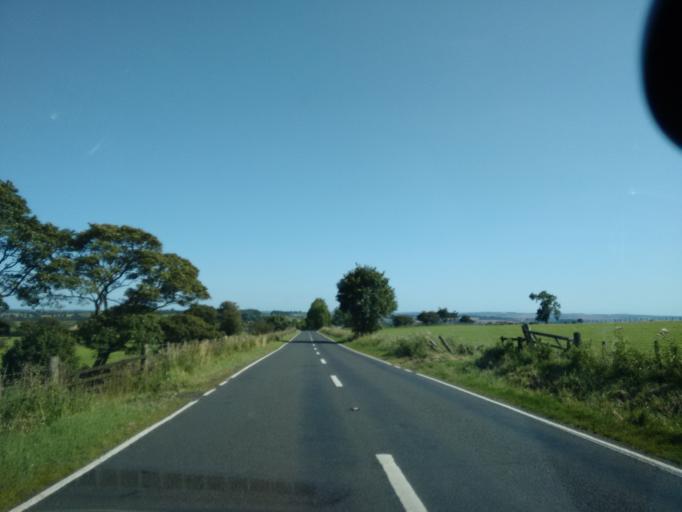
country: GB
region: England
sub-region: Northumberland
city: Corbridge
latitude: 55.0139
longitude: -2.0303
